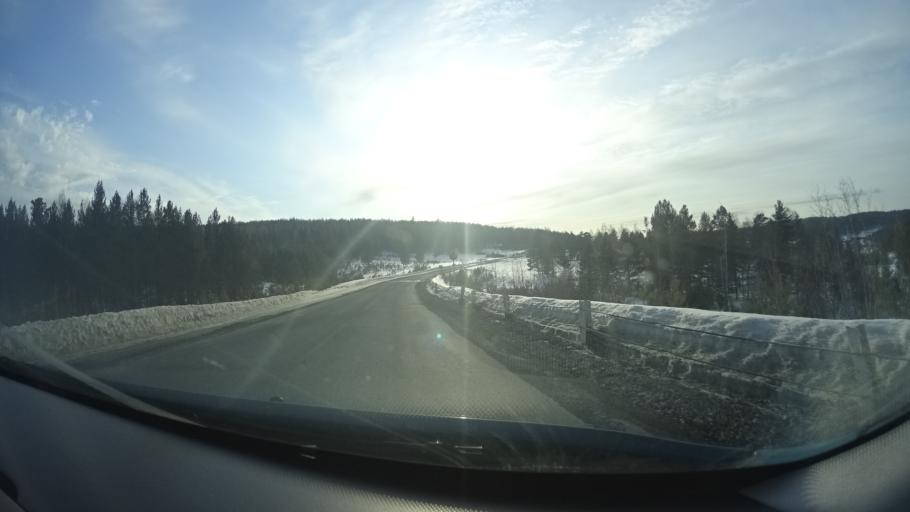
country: RU
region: Bashkortostan
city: Lomovka
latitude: 53.6728
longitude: 58.2415
